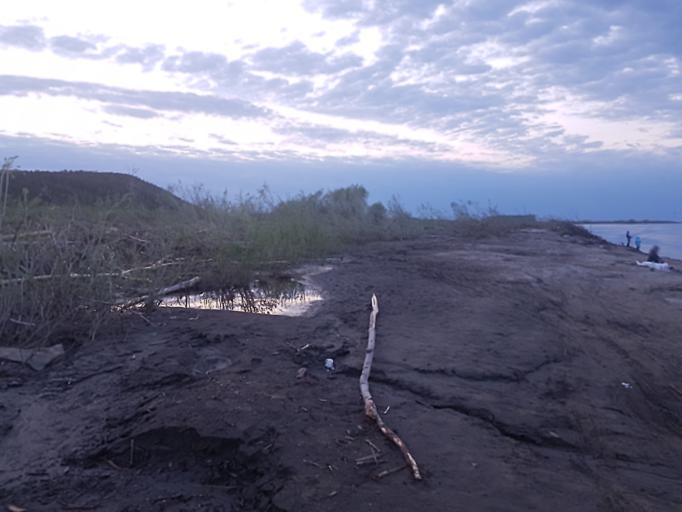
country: RU
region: Sakha
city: Tabaga
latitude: 61.8018
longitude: 129.6667
